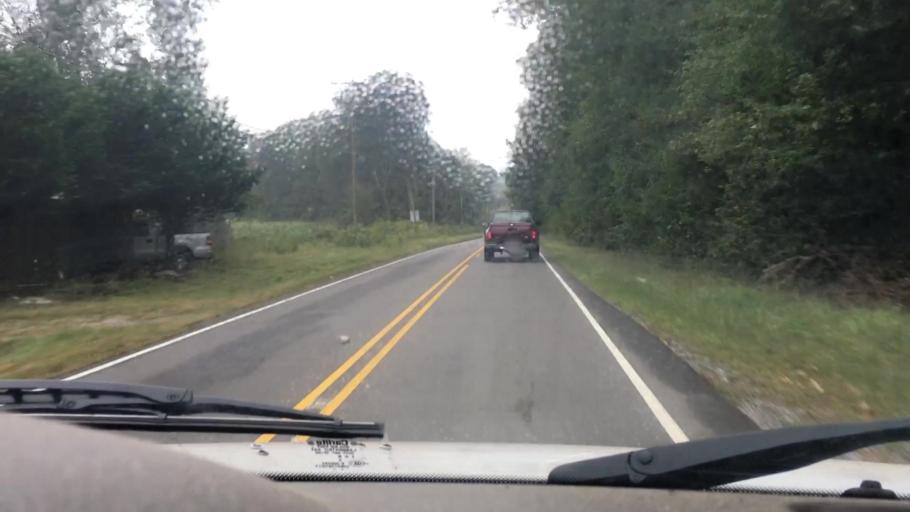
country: US
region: North Carolina
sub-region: Iredell County
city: Mooresville
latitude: 35.6272
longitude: -80.7804
